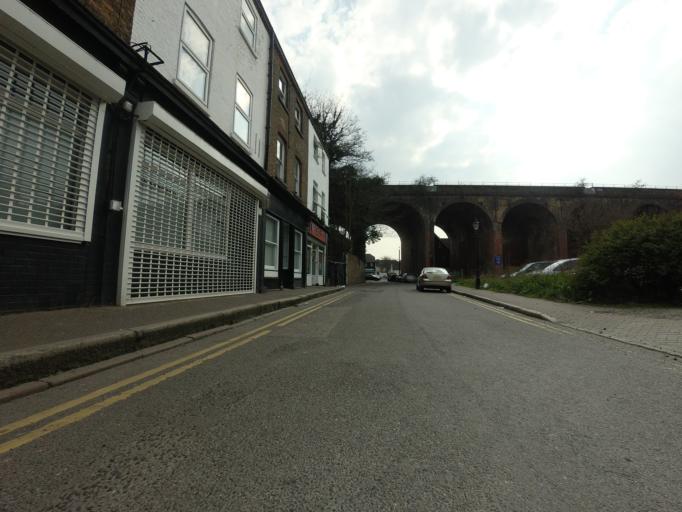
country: GB
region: England
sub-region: Greater London
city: Orpington
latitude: 51.3949
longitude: 0.1151
